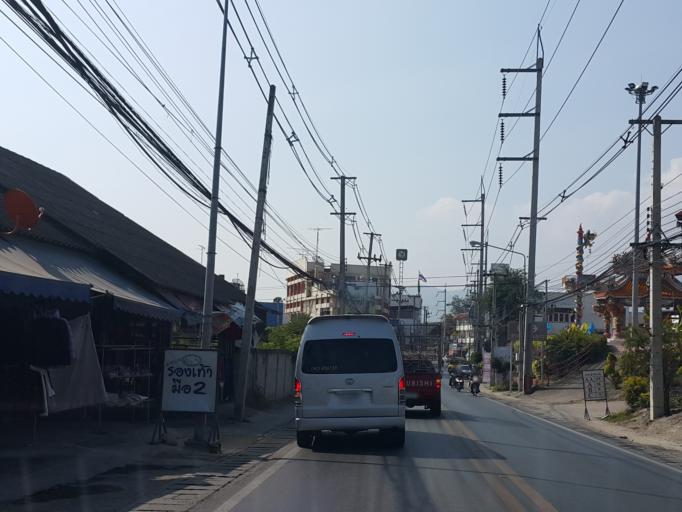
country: TH
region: Chiang Mai
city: Chom Thong
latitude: 18.4255
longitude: 98.6802
